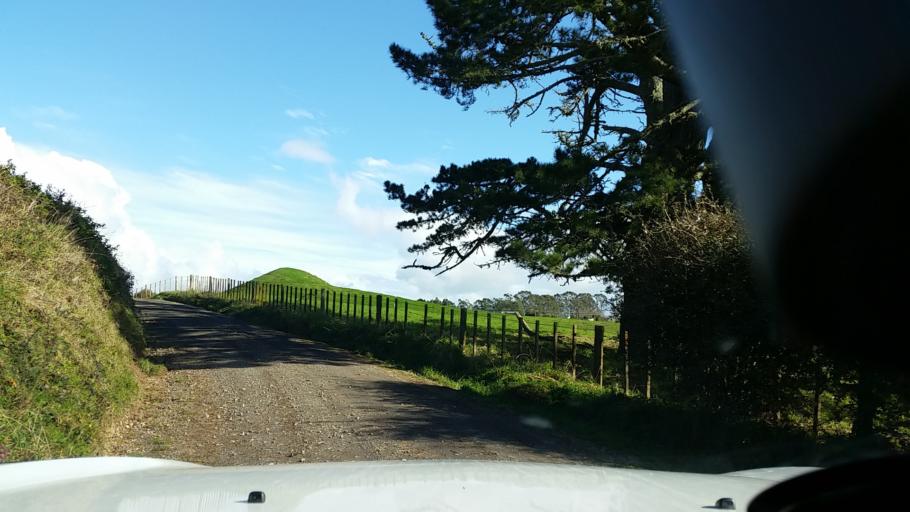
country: NZ
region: Bay of Plenty
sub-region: Rotorua District
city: Rotorua
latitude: -38.0236
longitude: 176.2849
